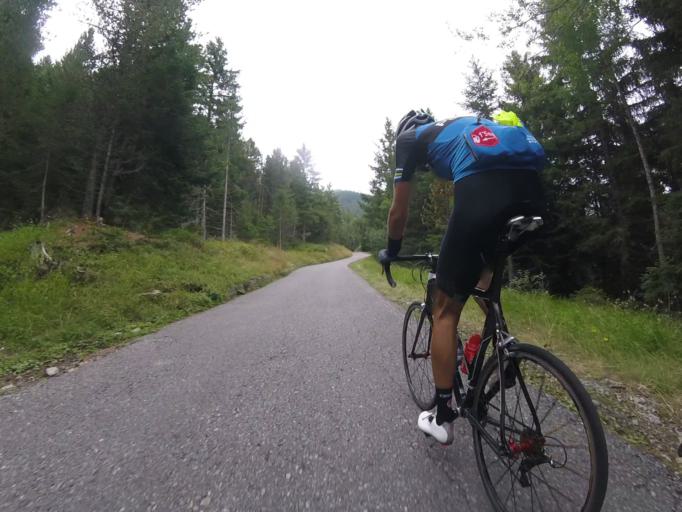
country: IT
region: Lombardy
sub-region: Provincia di Sondrio
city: Mazzo di Valtellina
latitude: 46.2492
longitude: 10.2886
